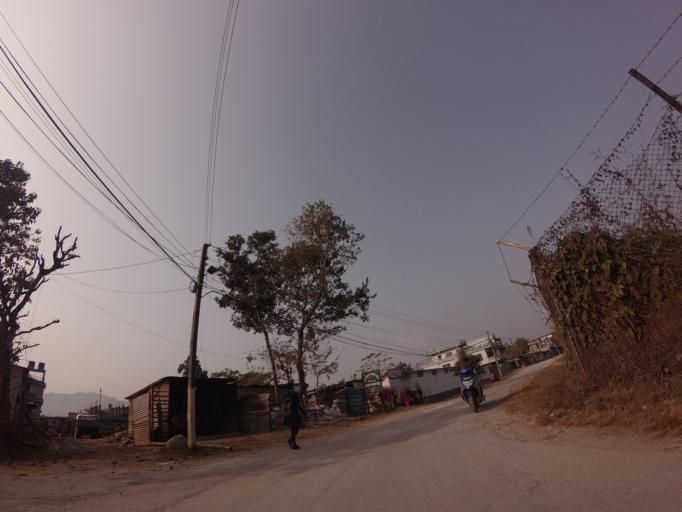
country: NP
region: Western Region
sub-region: Gandaki Zone
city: Pokhara
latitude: 28.1979
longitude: 83.9820
